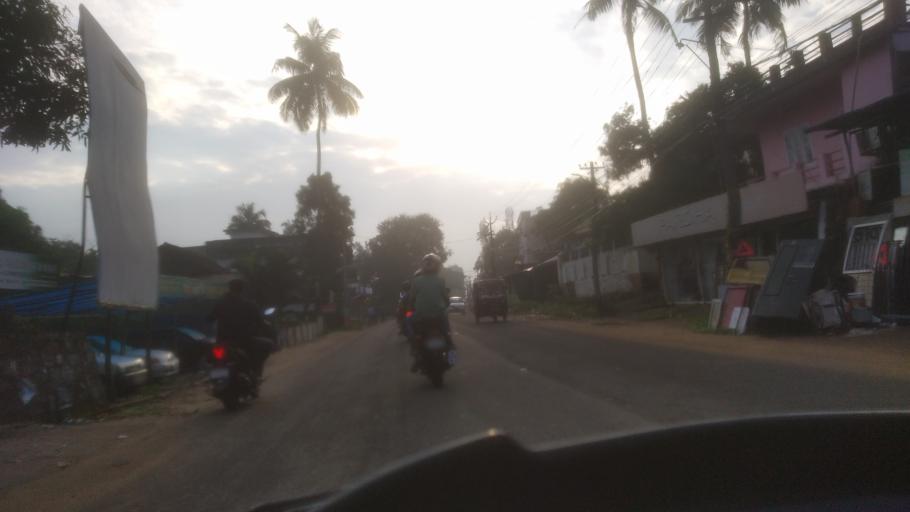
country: IN
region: Kerala
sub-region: Ernakulam
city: Perumpavur
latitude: 10.1161
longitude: 76.4607
